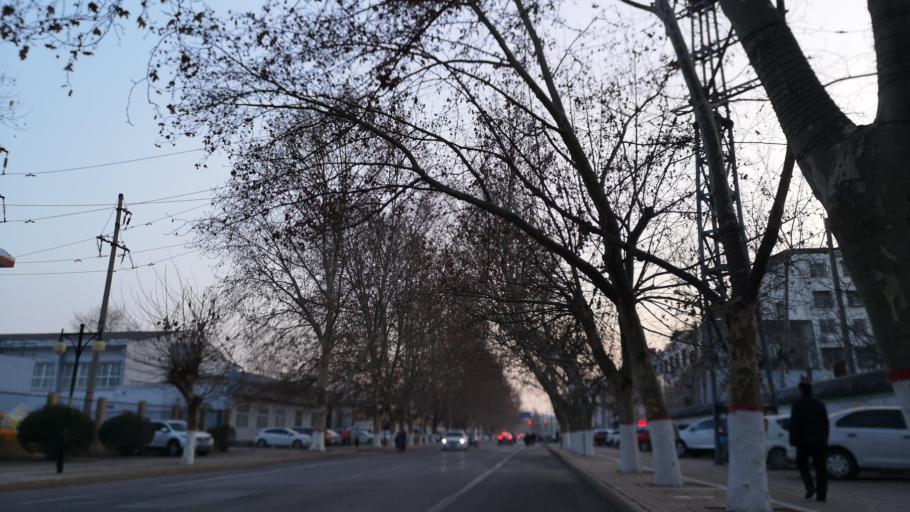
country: CN
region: Henan Sheng
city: Zhongyuanlu
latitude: 35.7706
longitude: 115.0749
